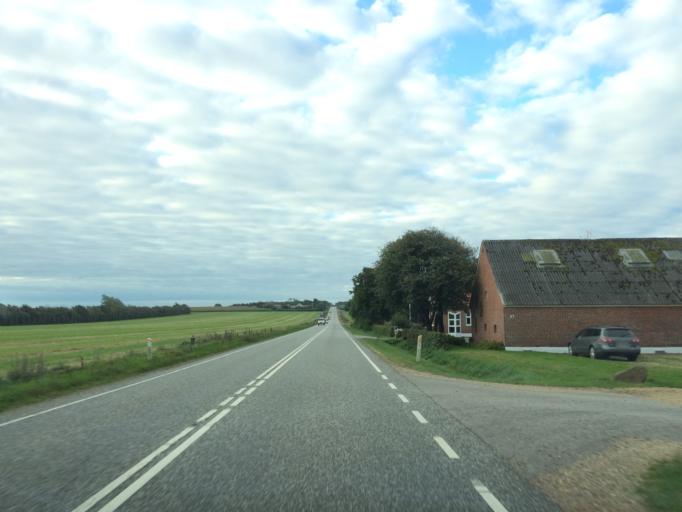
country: DK
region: Central Jutland
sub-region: Ringkobing-Skjern Kommune
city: Skjern
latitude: 56.0318
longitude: 8.5019
